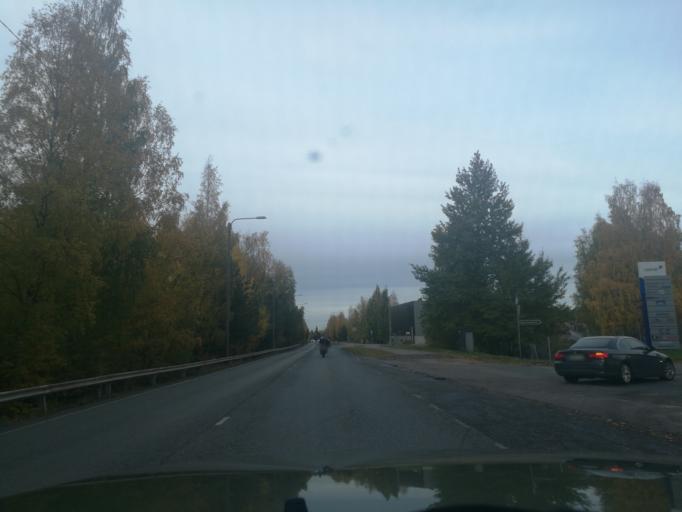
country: FI
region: Uusimaa
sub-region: Helsinki
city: Vantaa
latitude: 60.2997
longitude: 25.0871
